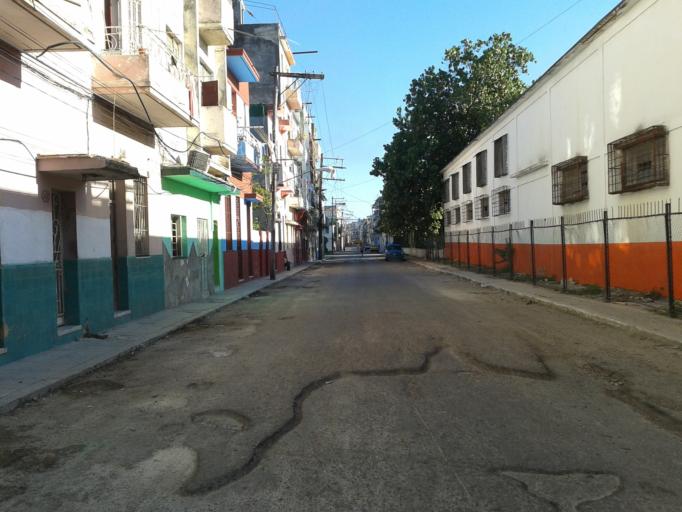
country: CU
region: La Habana
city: Havana
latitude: 23.1236
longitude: -82.3729
